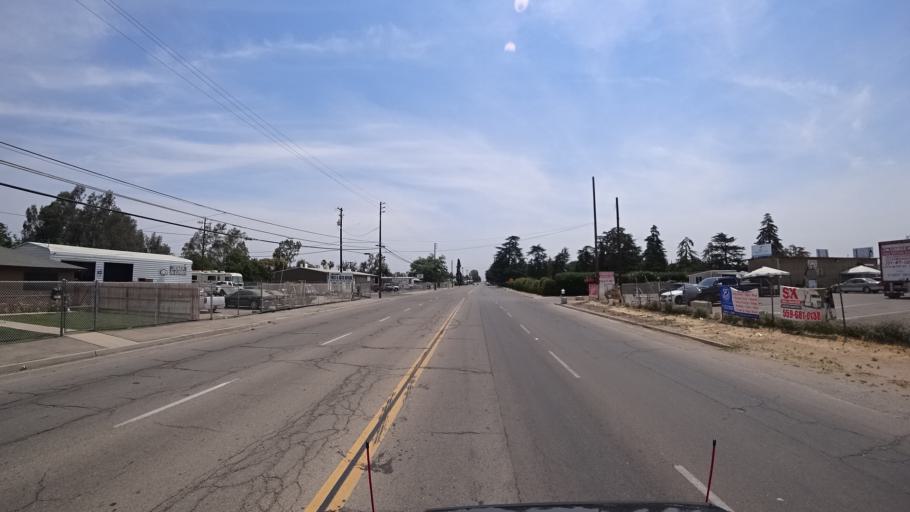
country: US
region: California
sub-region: Fresno County
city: West Park
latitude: 36.7502
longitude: -119.8384
